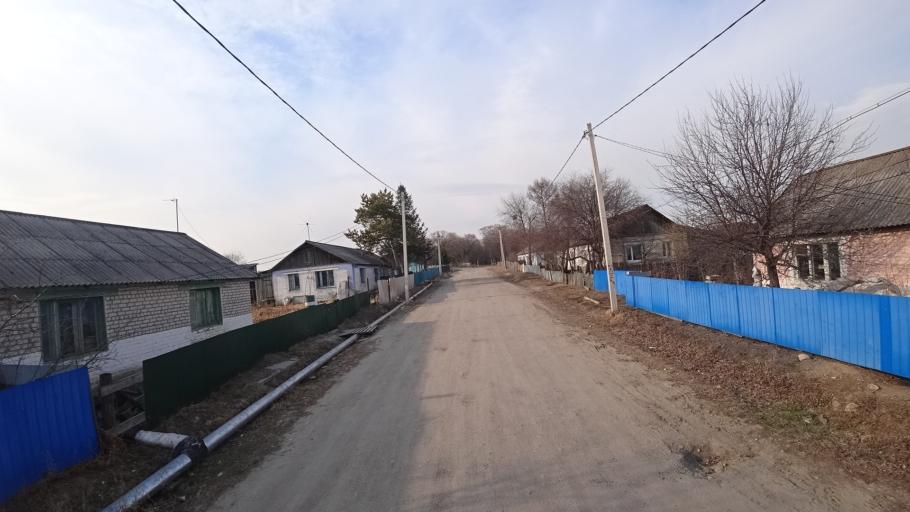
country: RU
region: Amur
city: Novobureyskiy
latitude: 49.8988
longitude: 129.8755
